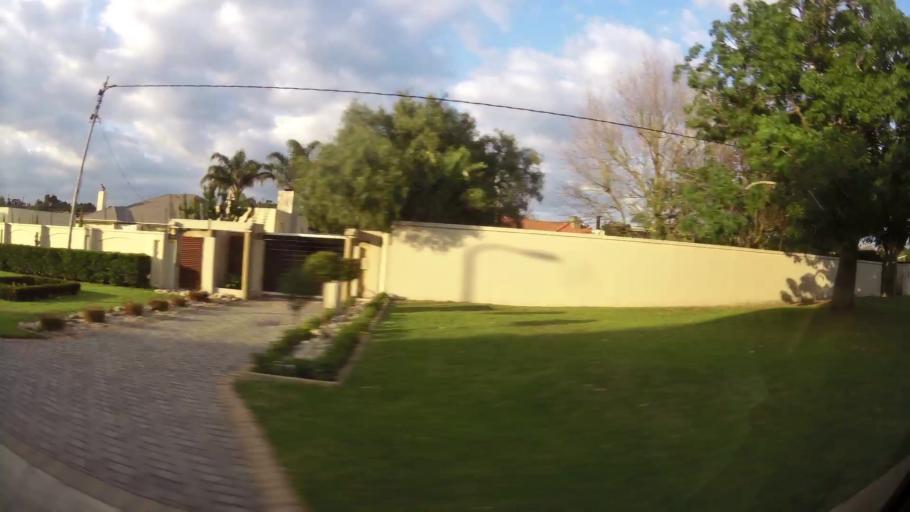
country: ZA
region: Eastern Cape
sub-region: Nelson Mandela Bay Metropolitan Municipality
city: Port Elizabeth
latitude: -33.9794
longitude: 25.5732
